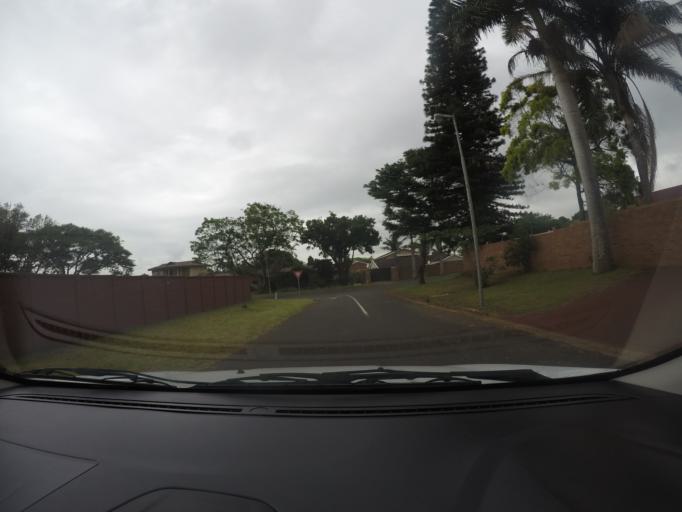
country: ZA
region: KwaZulu-Natal
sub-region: uThungulu District Municipality
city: Empangeni
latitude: -28.7631
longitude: 31.8953
